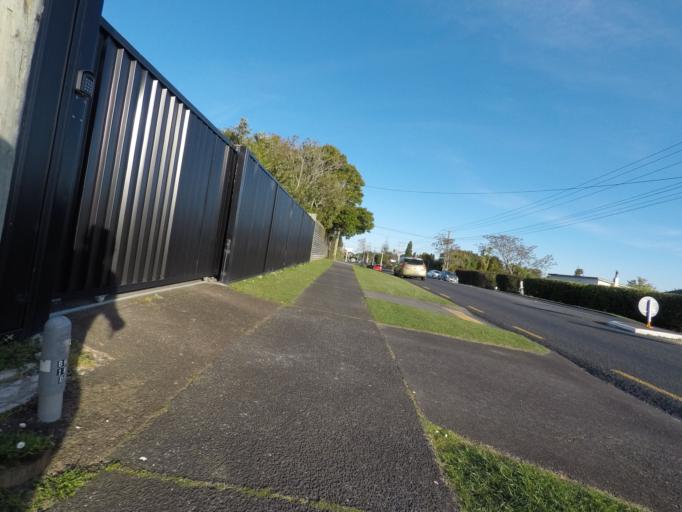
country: NZ
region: Auckland
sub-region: Auckland
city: Rosebank
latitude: -36.8406
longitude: 174.6442
